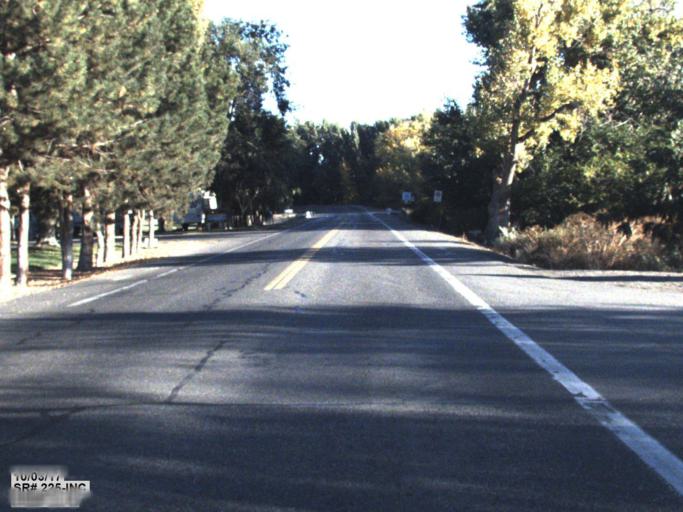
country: US
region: Washington
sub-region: Benton County
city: Benton City
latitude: 46.2543
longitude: -119.4754
